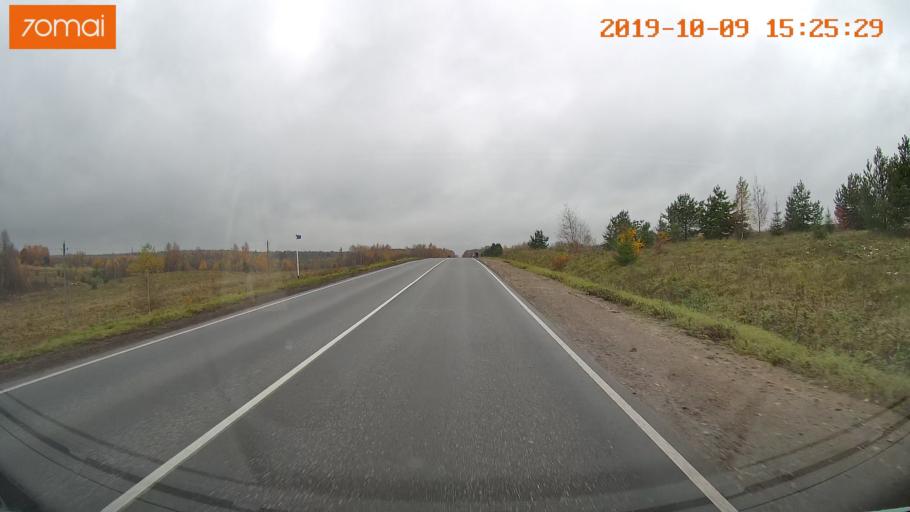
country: RU
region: Kostroma
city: Susanino
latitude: 58.0267
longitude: 41.4273
